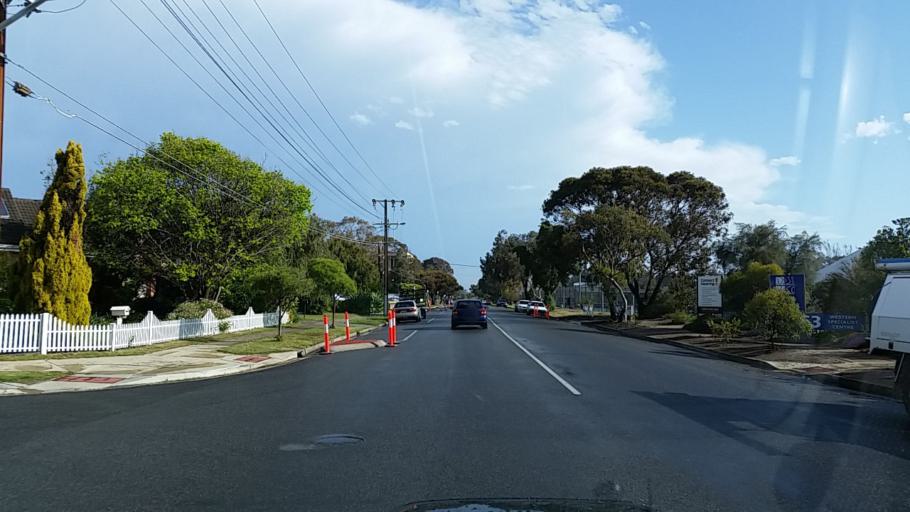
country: AU
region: South Australia
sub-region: Charles Sturt
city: Grange
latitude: -34.9089
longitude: 138.4991
